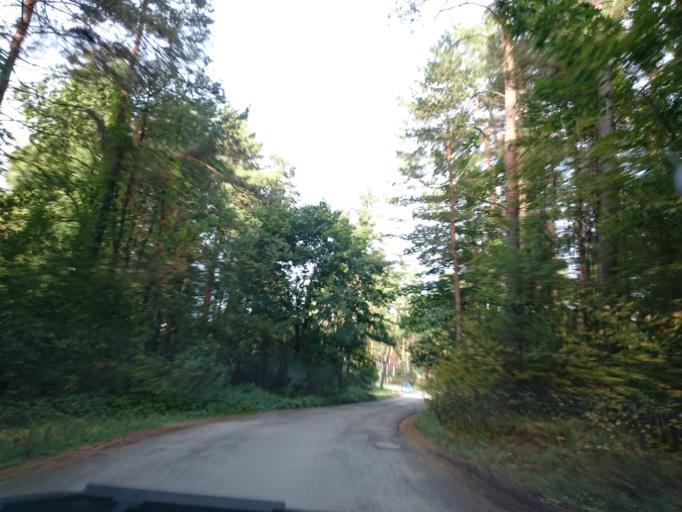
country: LV
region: Adazi
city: Adazi
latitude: 57.0385
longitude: 24.3313
